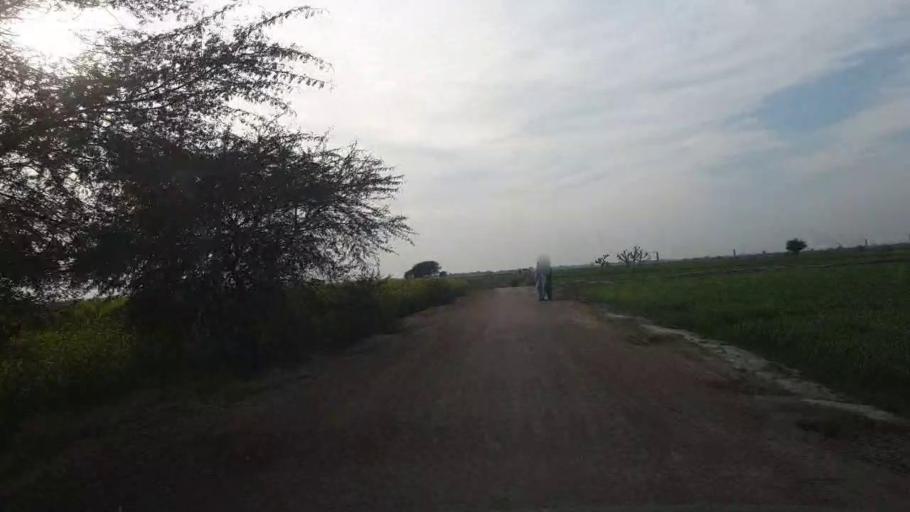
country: PK
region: Sindh
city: Shahpur Chakar
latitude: 26.1240
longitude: 68.5892
